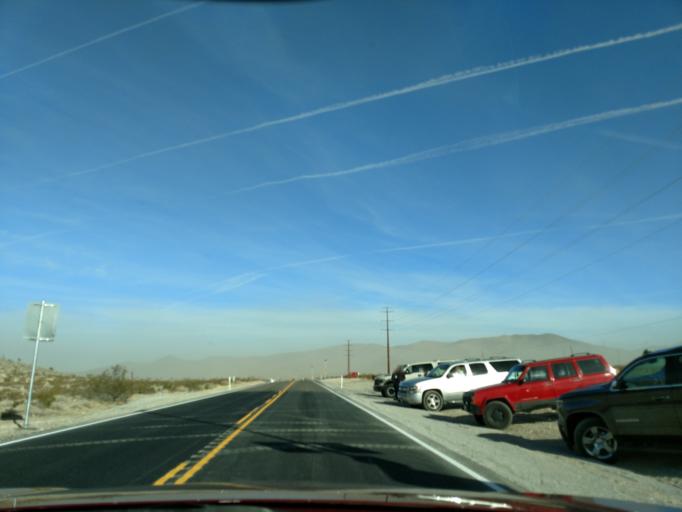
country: US
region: Nevada
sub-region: Nye County
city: Pahrump
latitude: 36.4287
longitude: -116.0711
